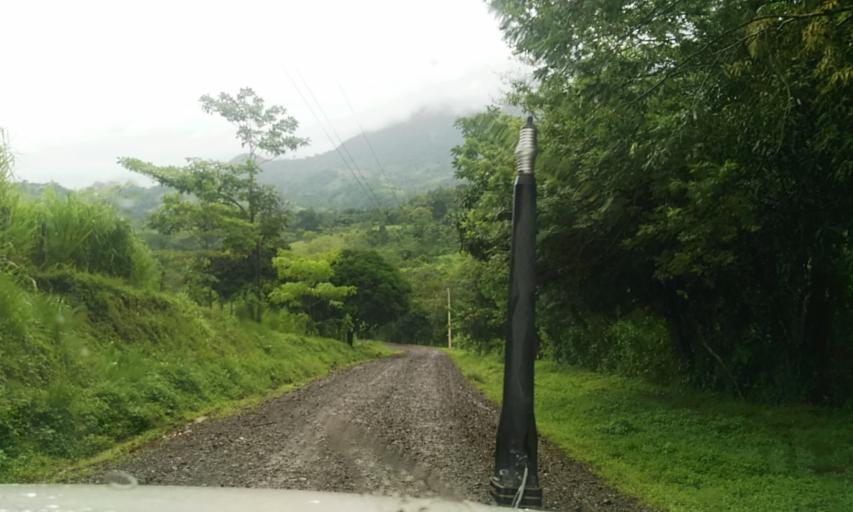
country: NI
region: Matagalpa
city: Rio Blanco
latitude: 13.0153
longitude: -85.2061
